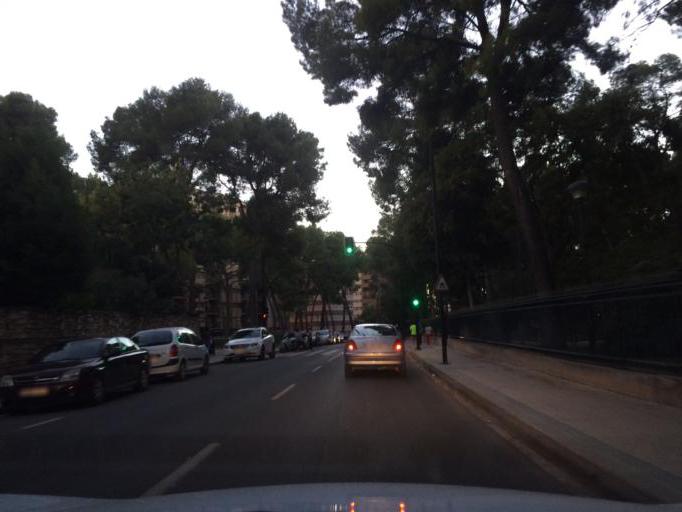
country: ES
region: Castille-La Mancha
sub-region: Provincia de Albacete
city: Albacete
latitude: 38.9860
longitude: -1.8559
